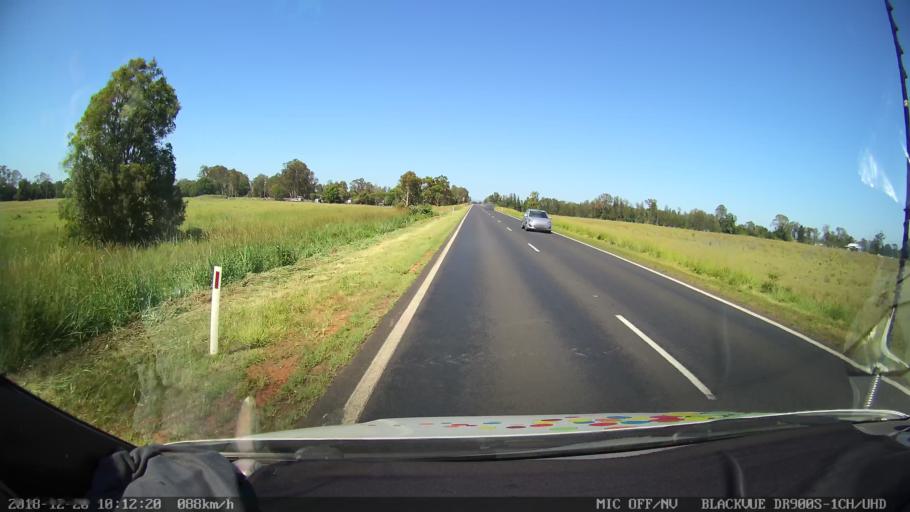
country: AU
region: New South Wales
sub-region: Richmond Valley
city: Casino
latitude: -28.8725
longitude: 153.1452
